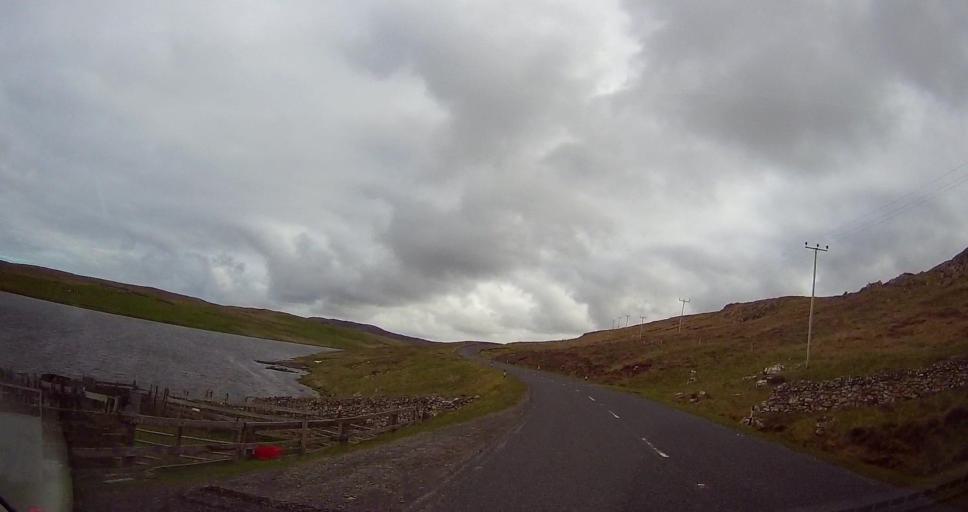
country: GB
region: Scotland
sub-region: Shetland Islands
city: Shetland
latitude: 60.6903
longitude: -0.9592
